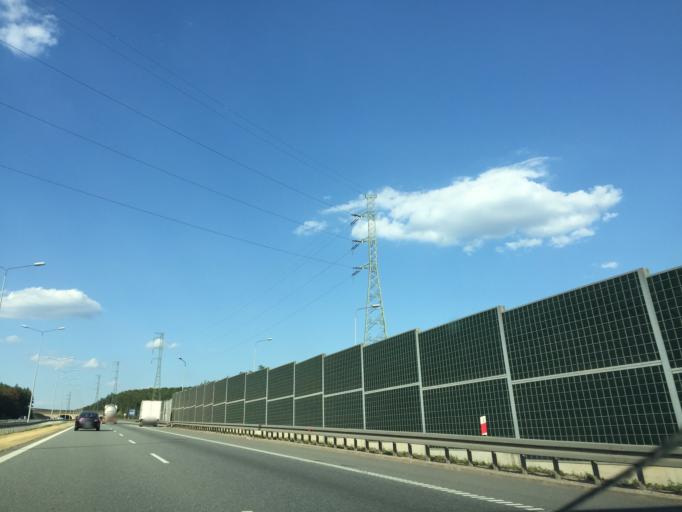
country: PL
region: Swietokrzyskie
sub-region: Powiat kielecki
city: Piekoszow
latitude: 50.8420
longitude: 20.4839
